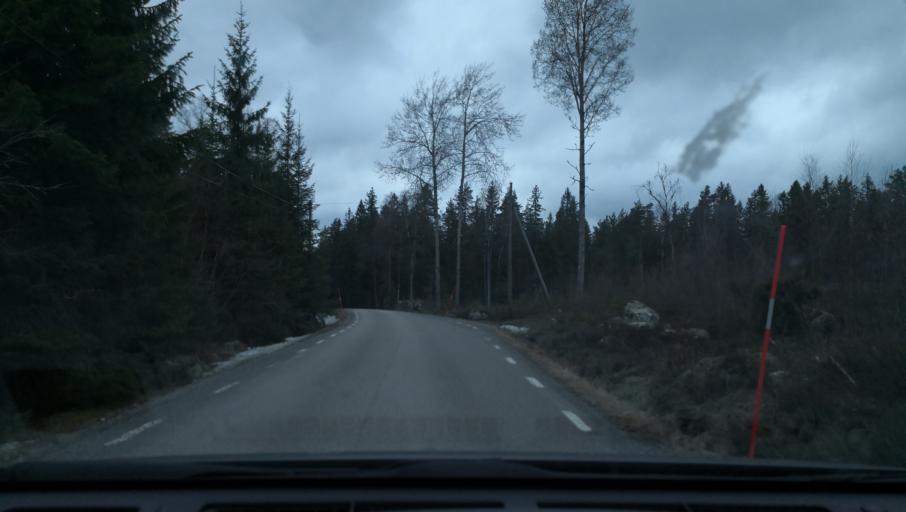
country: SE
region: Vaestmanland
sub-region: Kopings Kommun
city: Kolsva
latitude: 59.5732
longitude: 15.7173
